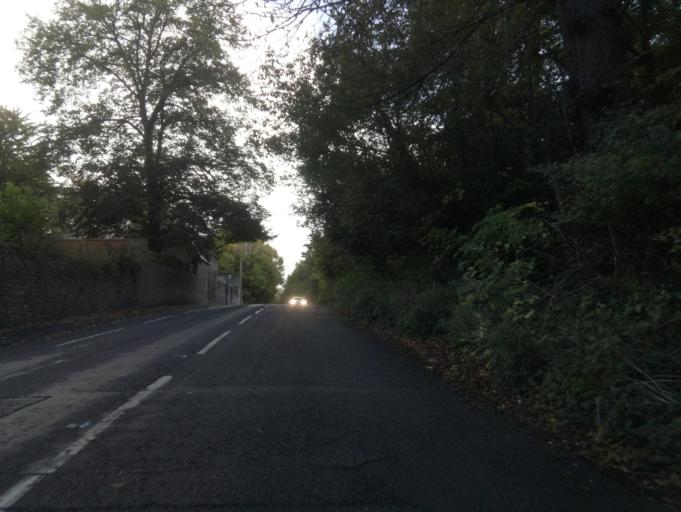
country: GB
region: England
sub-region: Bristol
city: Bristol
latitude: 51.5013
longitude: -2.6249
